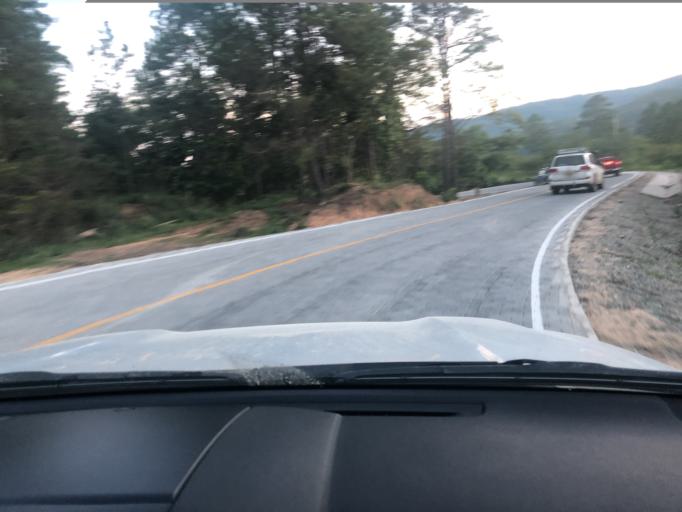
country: NI
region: Nueva Segovia
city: Ocotal
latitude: 13.6739
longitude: -86.6161
